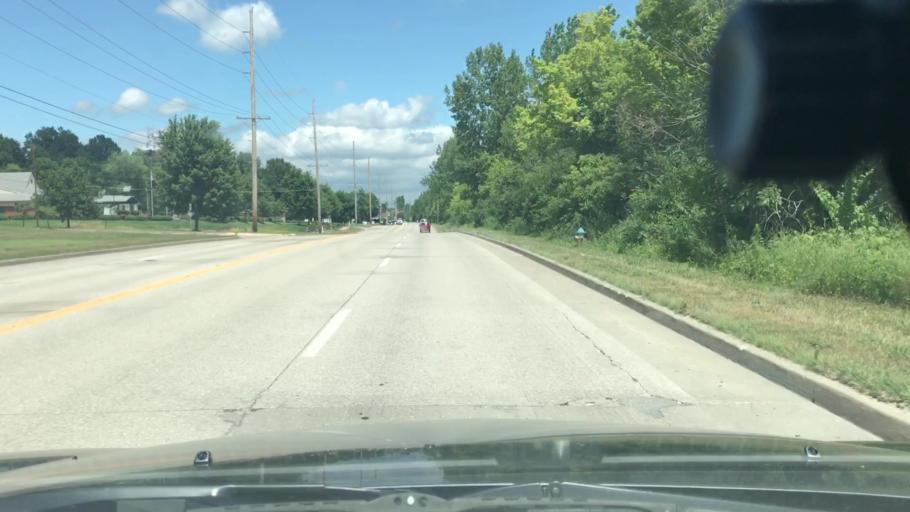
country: US
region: Missouri
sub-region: Saint Charles County
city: Saint Charles
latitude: 38.7567
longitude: -90.4993
